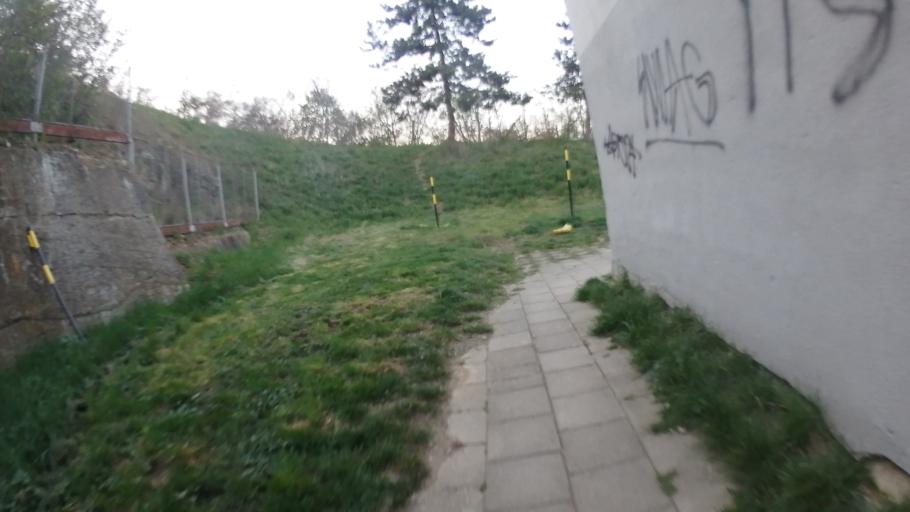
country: CZ
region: South Moravian
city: Ostopovice
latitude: 49.1811
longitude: 16.5592
